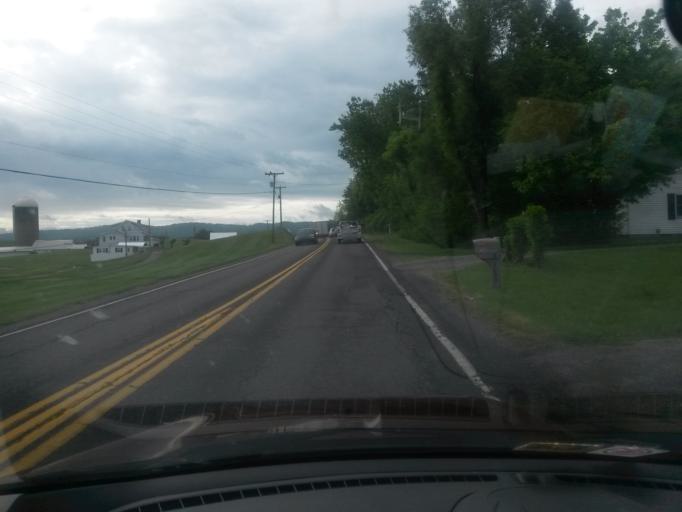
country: US
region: Virginia
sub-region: Montgomery County
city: Christiansburg
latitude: 37.0737
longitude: -80.4485
